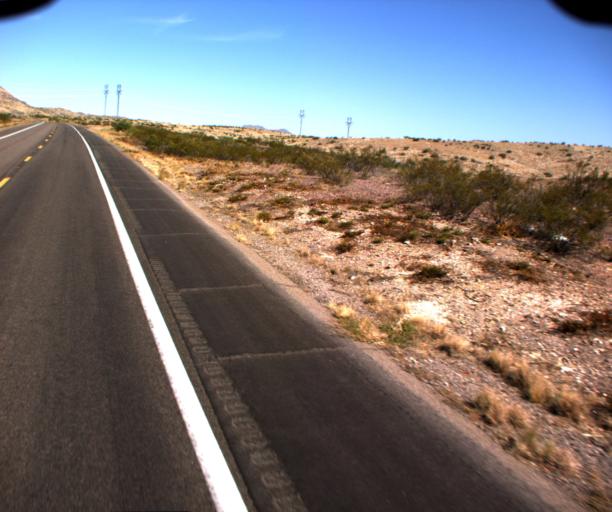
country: US
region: Arizona
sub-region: Greenlee County
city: Clifton
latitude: 32.7432
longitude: -109.2121
